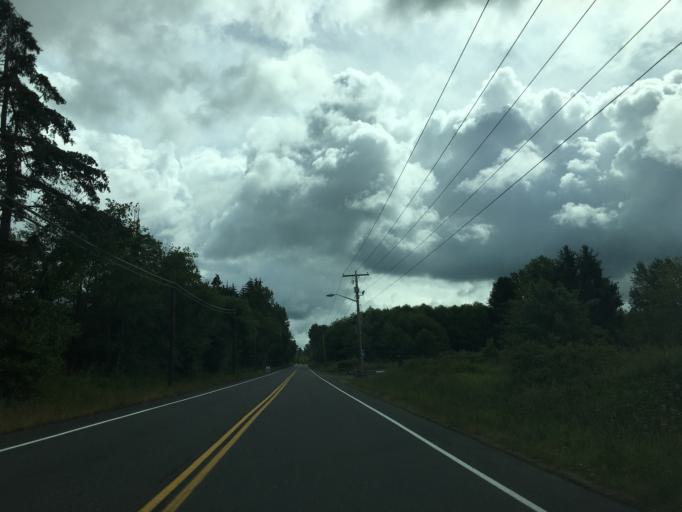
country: US
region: Washington
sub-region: Whatcom County
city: Birch Bay
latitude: 48.9177
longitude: -122.7352
